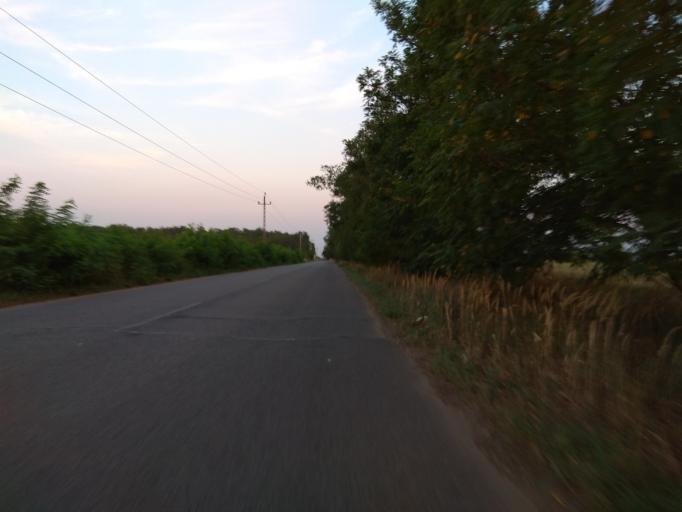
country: HU
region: Borsod-Abauj-Zemplen
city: Emod
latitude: 47.9109
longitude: 20.8524
